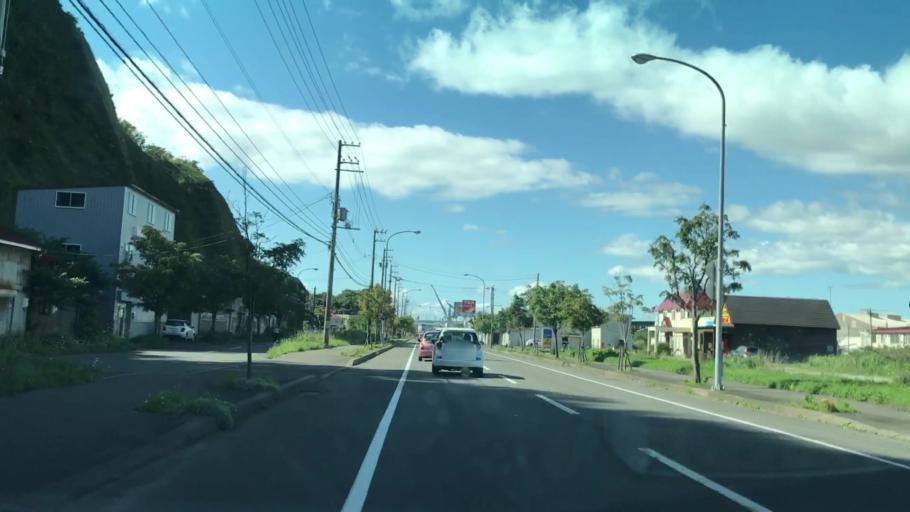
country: JP
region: Hokkaido
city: Muroran
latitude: 42.3301
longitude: 140.9664
